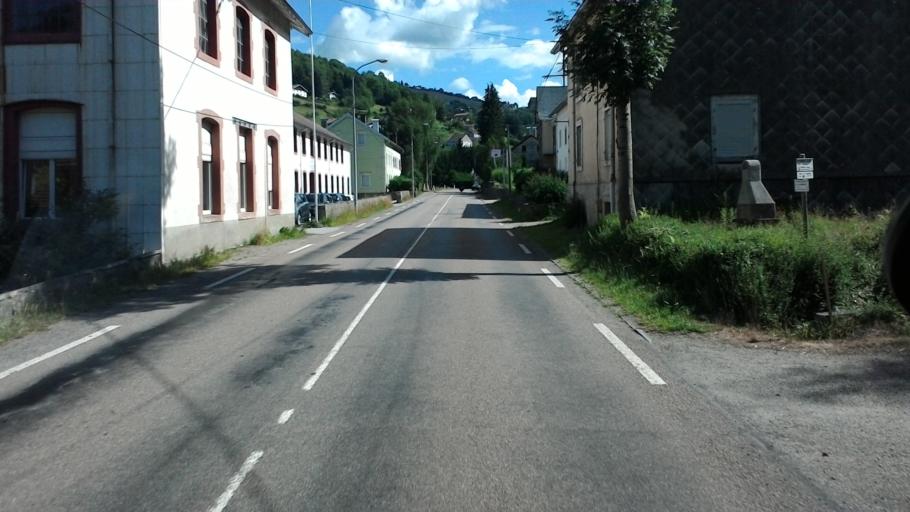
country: FR
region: Lorraine
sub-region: Departement des Vosges
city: La Bresse
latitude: 47.9913
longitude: 6.8491
